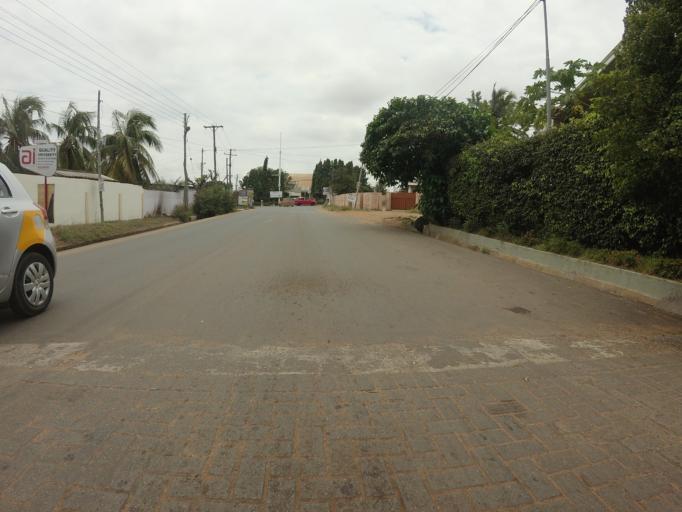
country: GH
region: Greater Accra
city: Nungua
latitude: 5.6071
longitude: -0.0940
